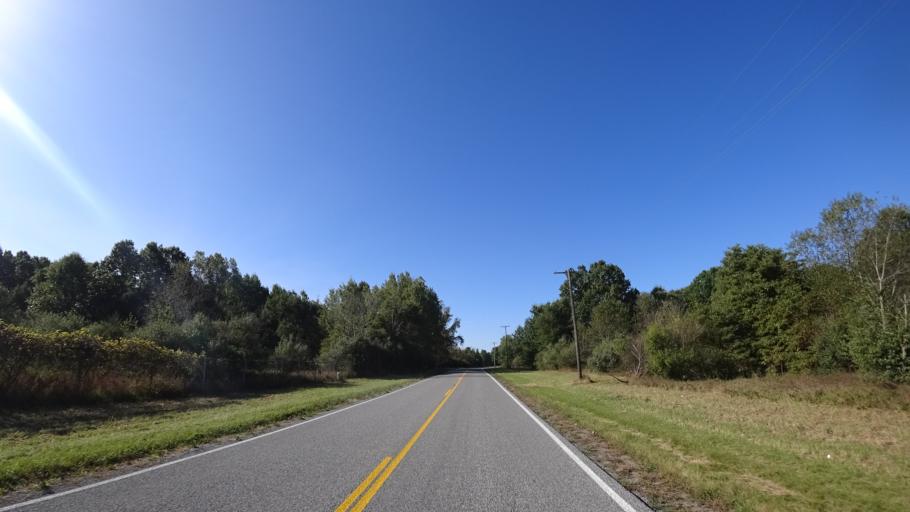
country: US
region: Michigan
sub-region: Berrien County
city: Benton Heights
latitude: 42.1500
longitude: -86.4260
